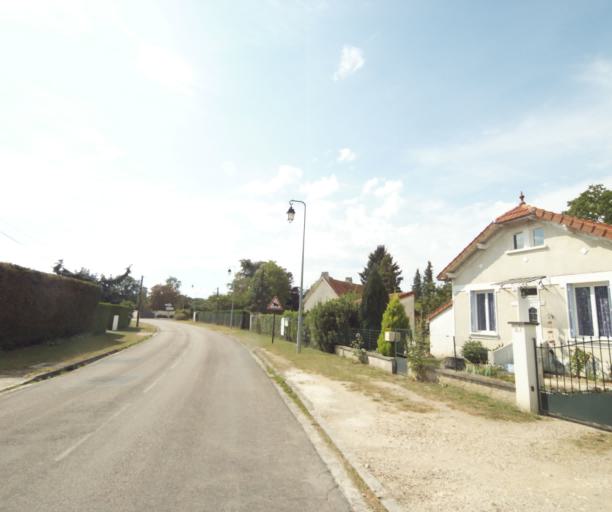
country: FR
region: Ile-de-France
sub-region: Departement de Seine-et-Marne
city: Acheres-la-Foret
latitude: 48.3566
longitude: 2.5639
